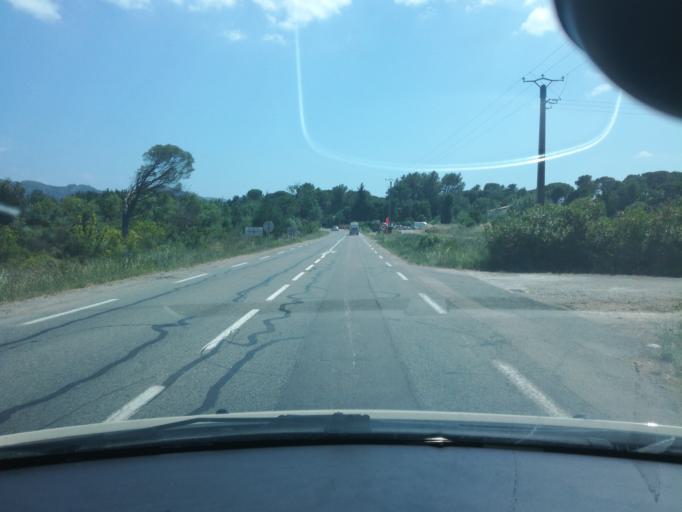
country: FR
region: Provence-Alpes-Cote d'Azur
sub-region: Departement du Var
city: Le Muy
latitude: 43.4904
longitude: 6.5652
